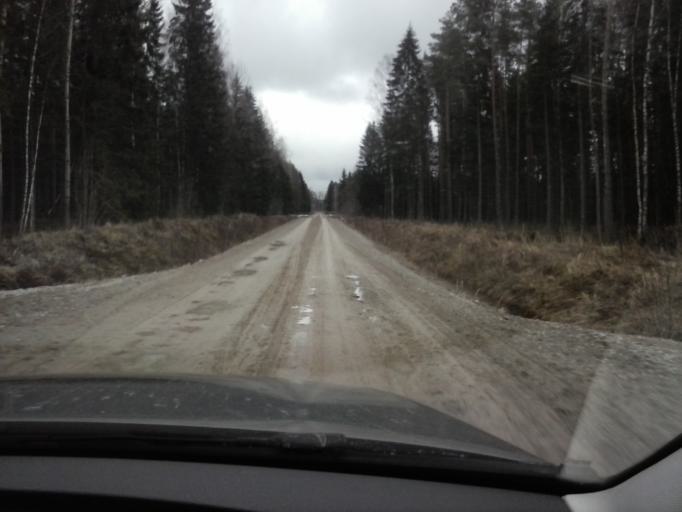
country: EE
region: Jogevamaa
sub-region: Mustvee linn
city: Mustvee
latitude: 59.0601
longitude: 26.8507
